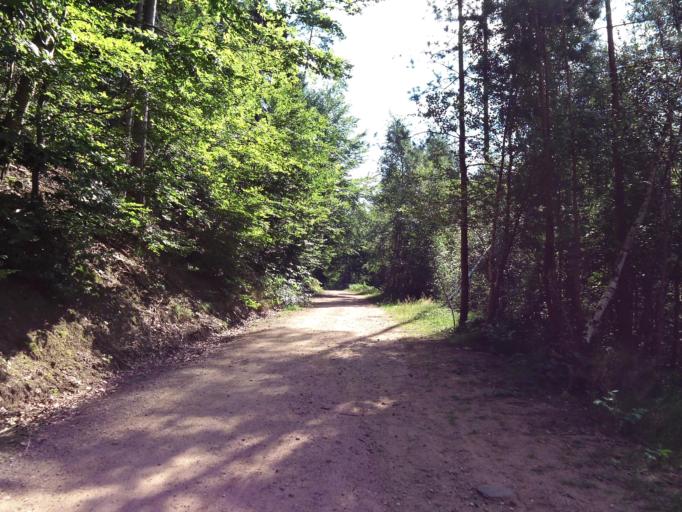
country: DE
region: Rheinland-Pfalz
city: Breunigweiler
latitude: 49.5437
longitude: 7.9575
